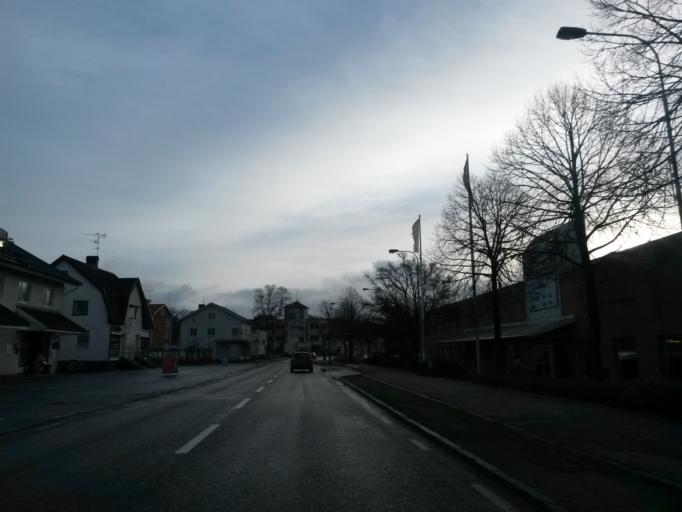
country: SE
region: Vaestra Goetaland
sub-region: Marks Kommun
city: Kinna
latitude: 57.4883
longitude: 12.6439
